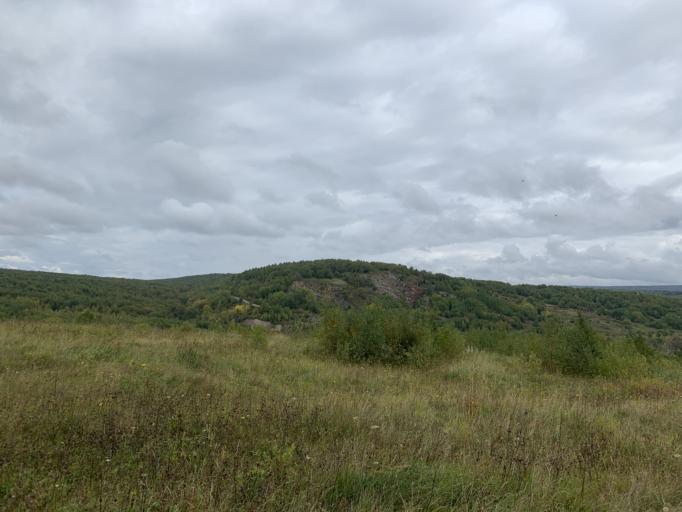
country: RU
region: Perm
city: Gubakha
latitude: 58.8733
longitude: 57.6057
